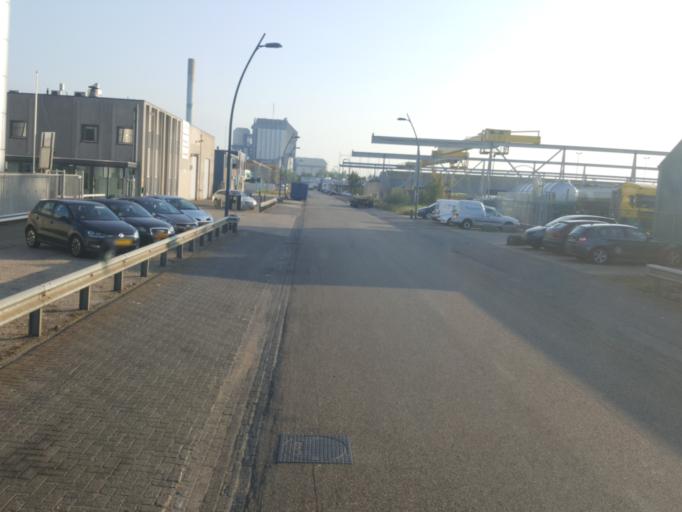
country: NL
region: Gelderland
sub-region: Gemeente Nijmegen
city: Nijmegen
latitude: 51.8480
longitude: 5.8243
